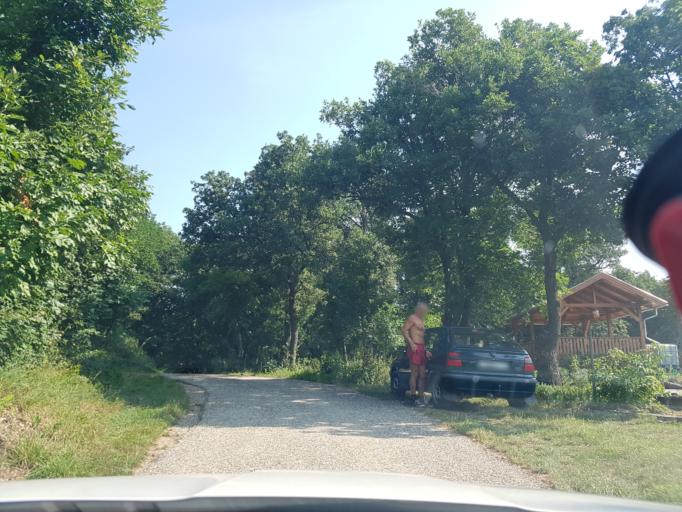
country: HU
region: Veszprem
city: Balatonalmadi
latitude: 47.0045
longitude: 17.9900
